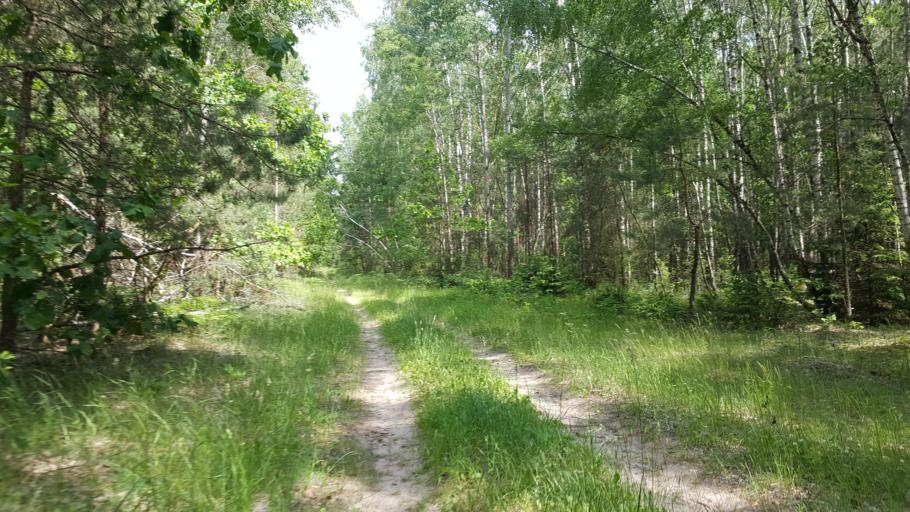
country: BY
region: Brest
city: Kamyanyuki
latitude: 52.4979
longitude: 23.8392
